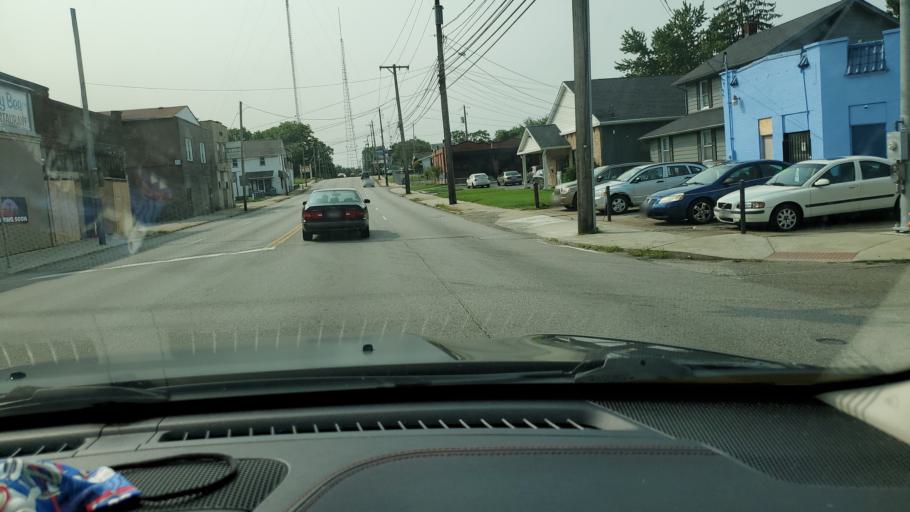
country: US
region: Ohio
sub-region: Mahoning County
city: Youngstown
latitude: 41.0663
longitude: -80.6462
